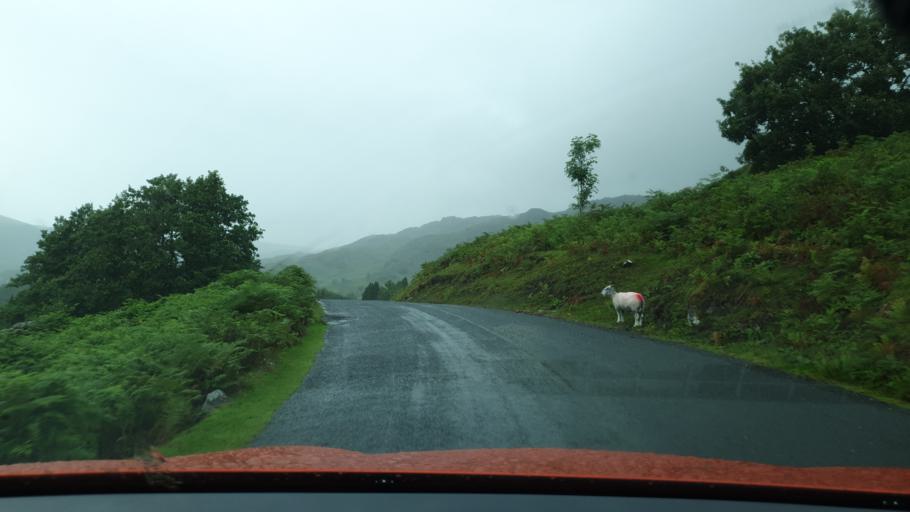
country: GB
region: England
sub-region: Cumbria
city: Millom
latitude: 54.3080
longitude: -3.2285
